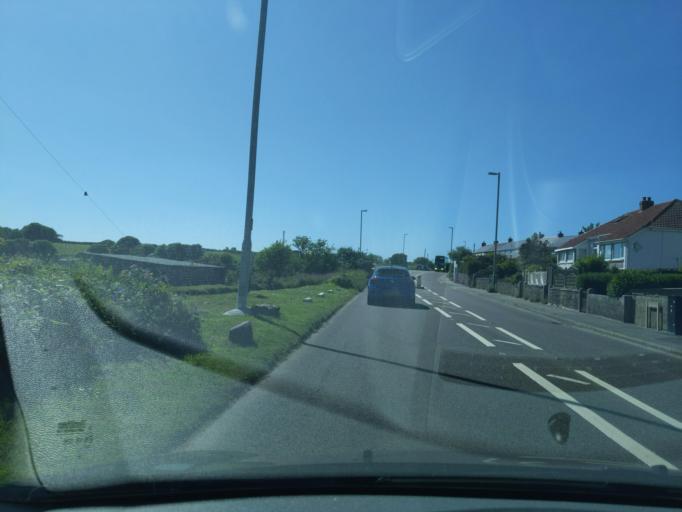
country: GB
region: England
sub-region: Cornwall
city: Penryn
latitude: 50.1642
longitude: -5.1598
